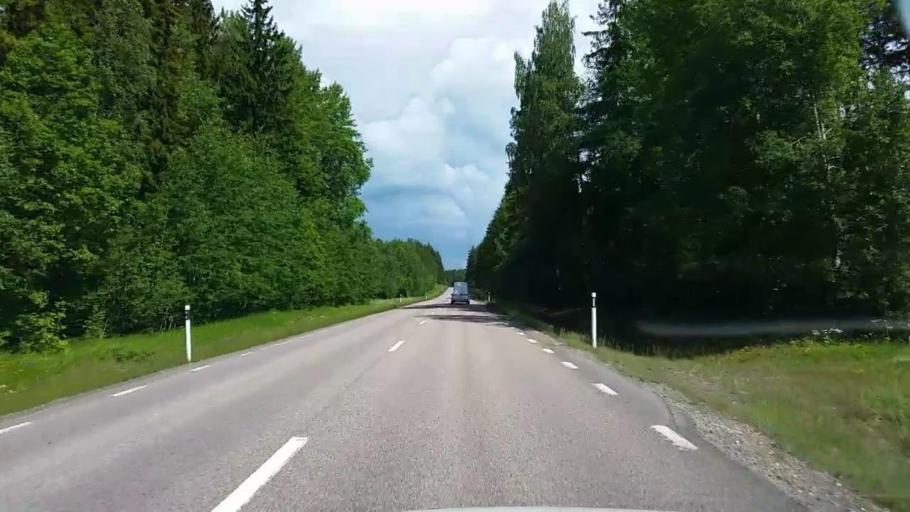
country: SE
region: Dalarna
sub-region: Avesta Kommun
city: Avesta
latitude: 60.1688
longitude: 16.2779
